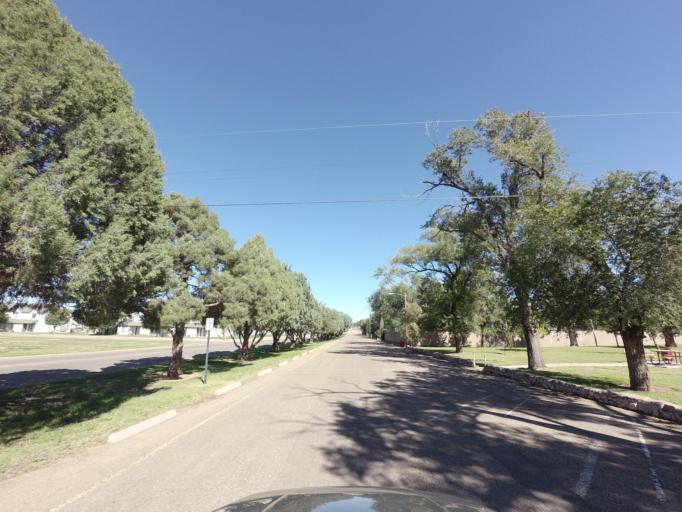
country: US
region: New Mexico
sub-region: Curry County
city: Clovis
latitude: 34.4084
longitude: -103.1875
